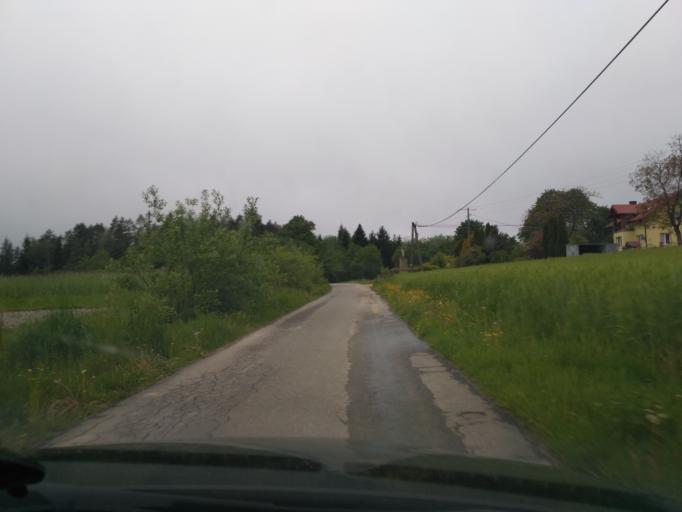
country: PL
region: Subcarpathian Voivodeship
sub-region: Powiat debicki
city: Jodlowa
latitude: 49.8570
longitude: 21.2429
